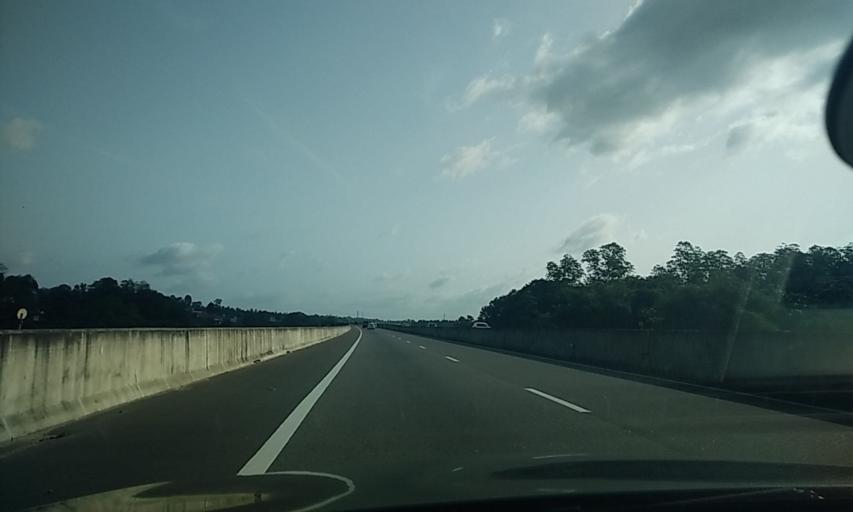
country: LK
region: Western
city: Homagama
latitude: 6.8968
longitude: 79.9788
